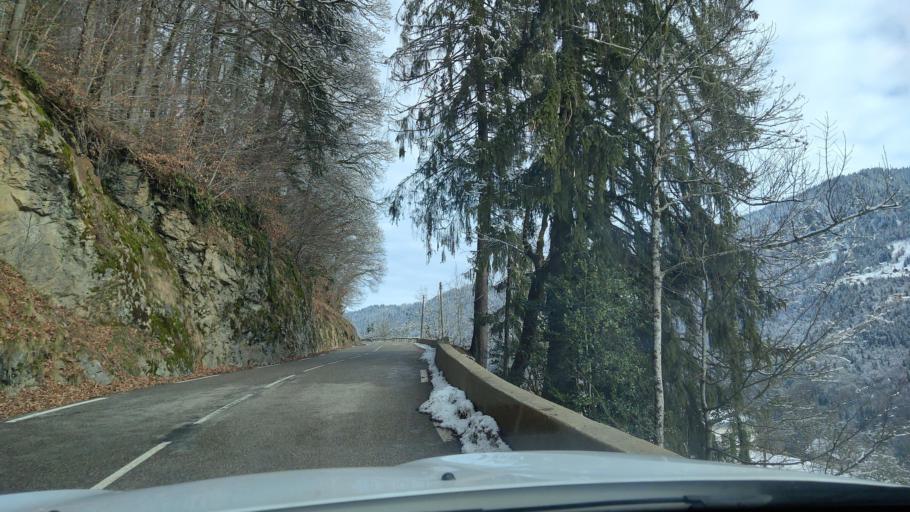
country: FR
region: Rhone-Alpes
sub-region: Departement de la Savoie
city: Ugine
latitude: 45.7669
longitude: 6.4698
